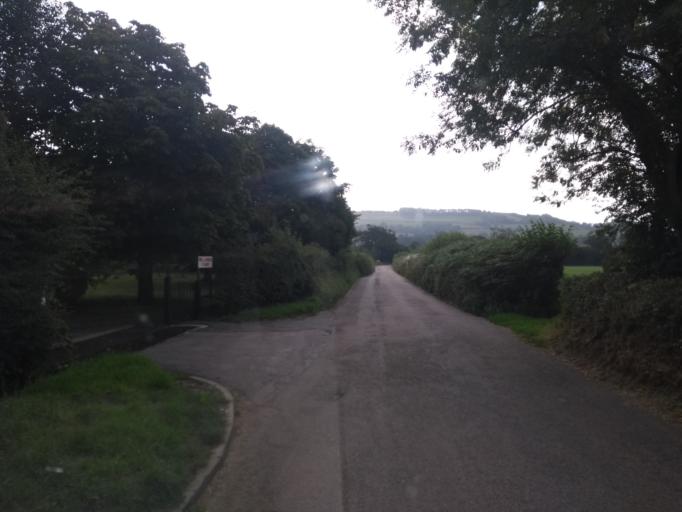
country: GB
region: England
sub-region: Devon
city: Colyton
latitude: 50.7512
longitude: -3.0404
